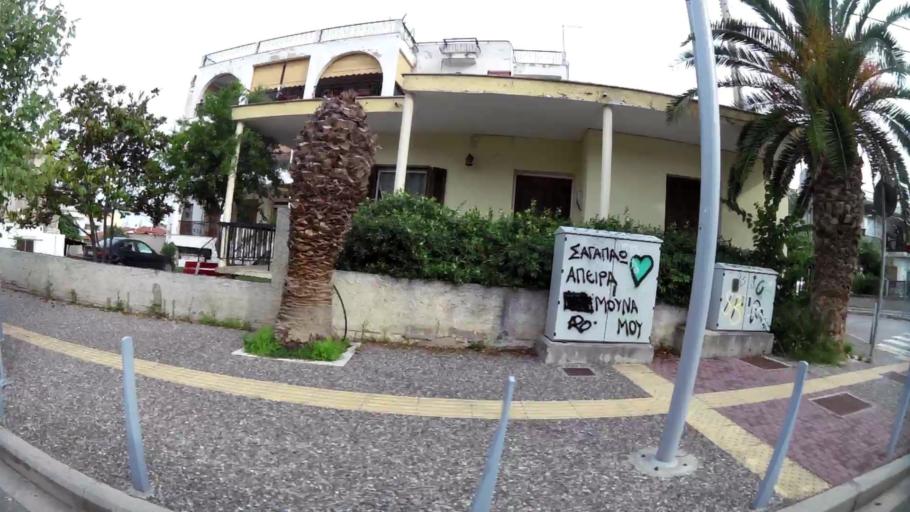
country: GR
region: Central Macedonia
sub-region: Nomos Thessalonikis
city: Thermi
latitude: 40.5501
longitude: 23.0251
